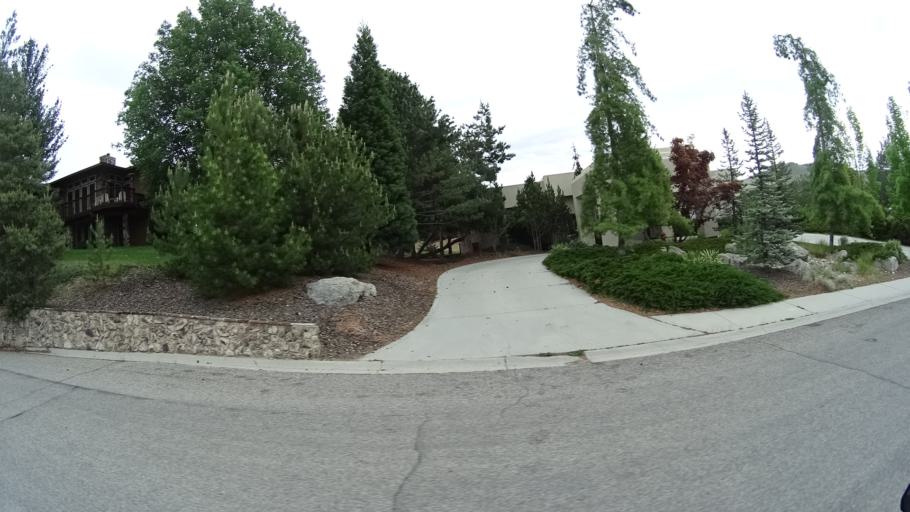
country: US
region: Idaho
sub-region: Ada County
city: Boise
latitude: 43.6161
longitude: -116.1715
